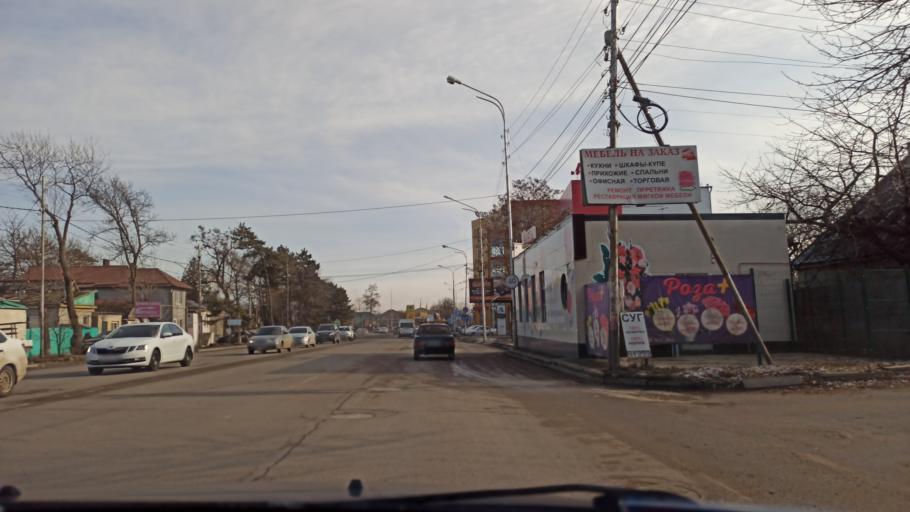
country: RU
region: Stavropol'skiy
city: Yessentuki
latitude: 44.0387
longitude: 42.8678
